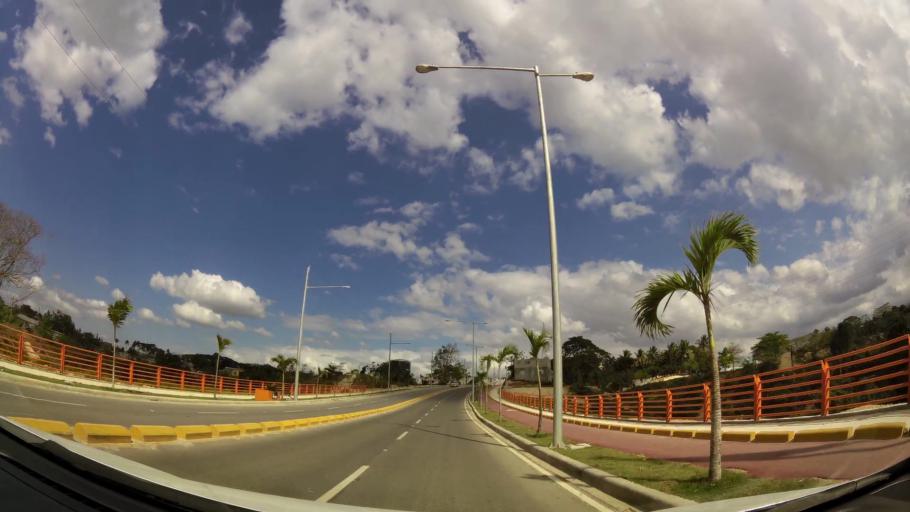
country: DO
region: Nacional
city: Ensanche Luperon
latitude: 18.5346
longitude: -69.8882
